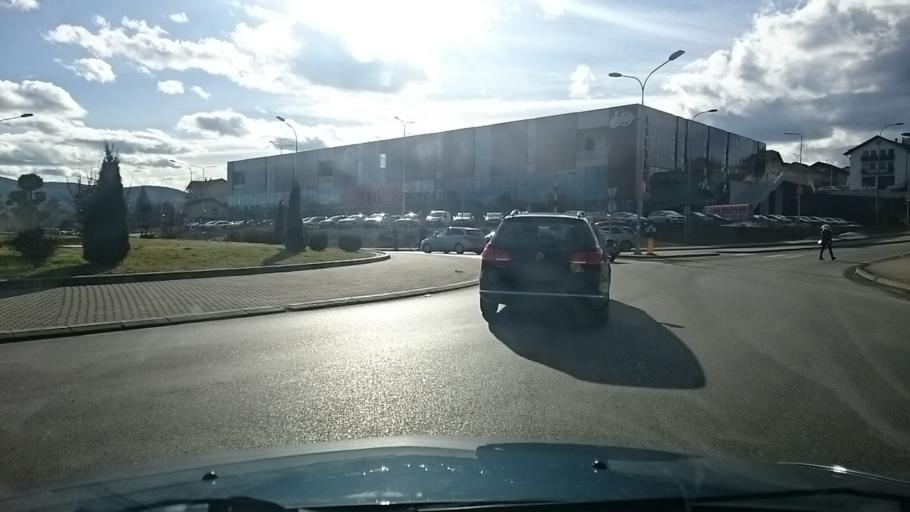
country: BA
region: Republika Srpska
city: Banja Luka
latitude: 44.7909
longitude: 17.1991
